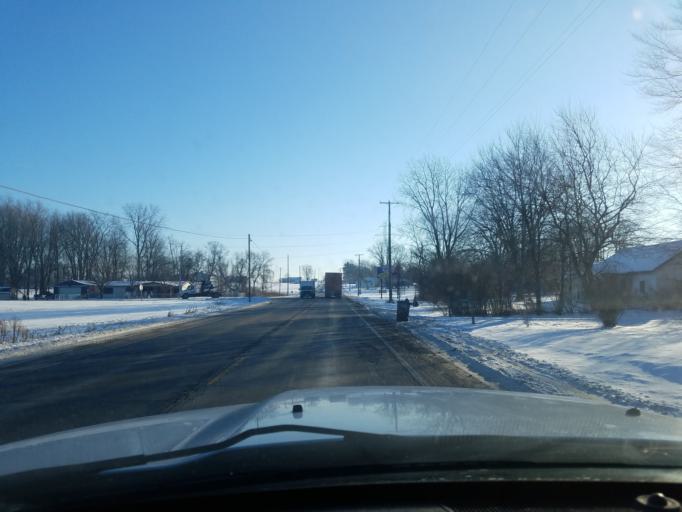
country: US
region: Indiana
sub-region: Noble County
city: Rome City
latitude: 41.4530
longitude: -85.3912
